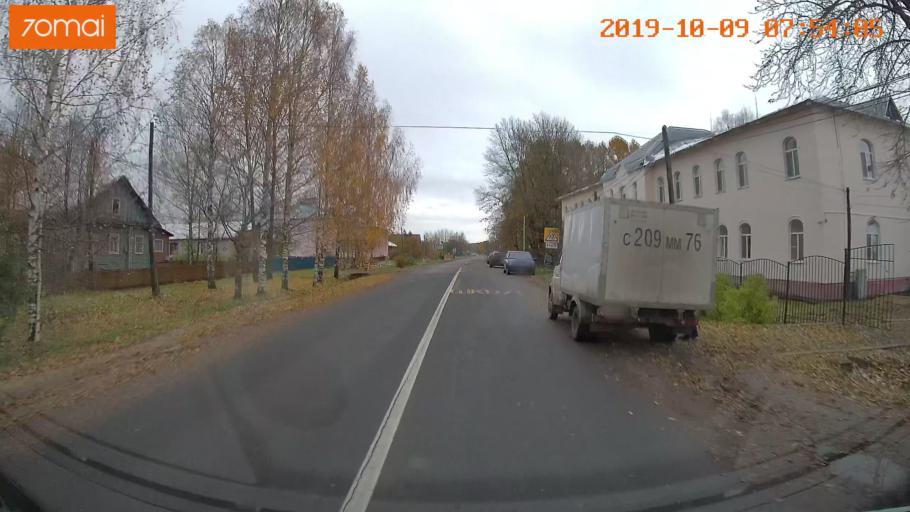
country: RU
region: Jaroslavl
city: Kukoboy
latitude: 58.6984
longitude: 39.9035
